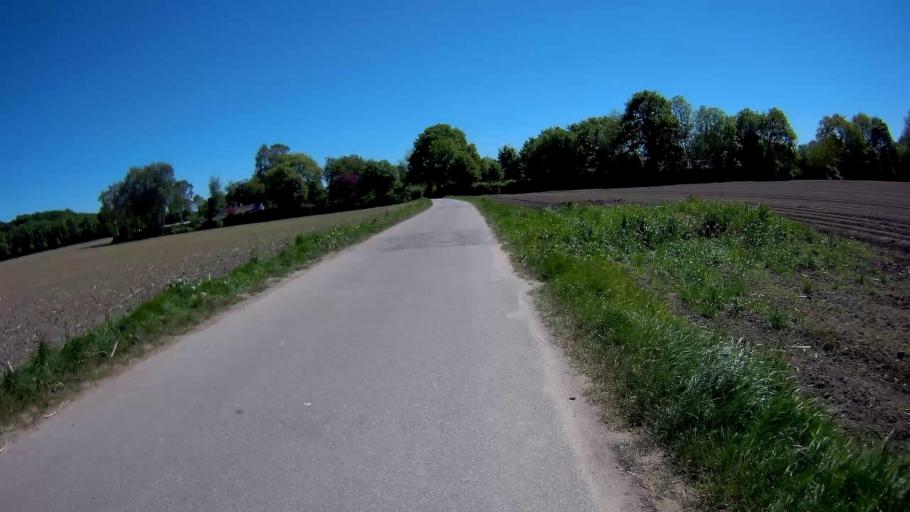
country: DE
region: North Rhine-Westphalia
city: Marl
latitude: 51.6046
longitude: 7.0633
